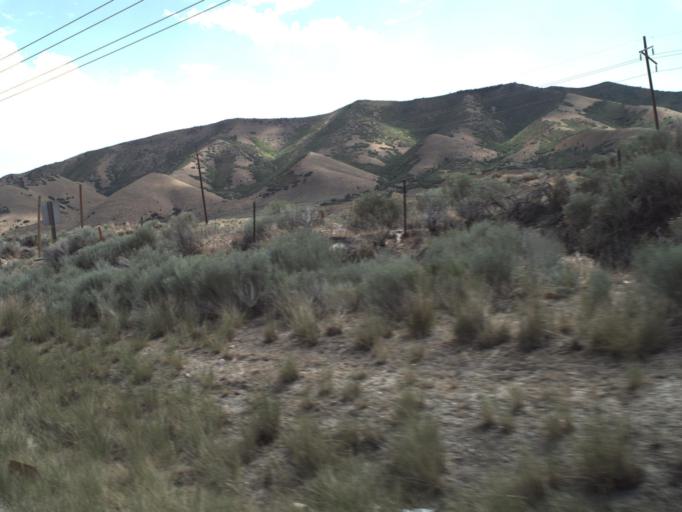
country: US
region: Utah
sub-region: Tooele County
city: Tooele
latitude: 40.4845
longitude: -112.3401
